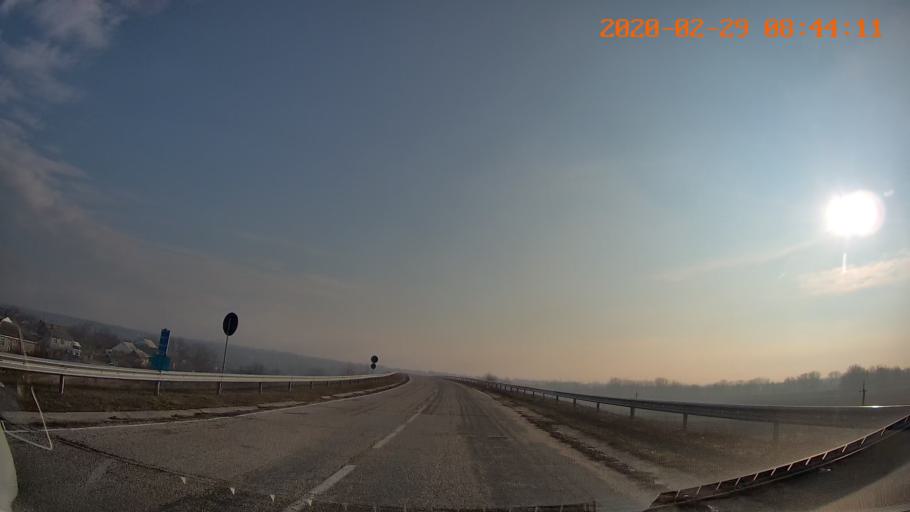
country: MD
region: Anenii Noi
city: Varnita
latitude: 46.9196
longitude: 29.4624
